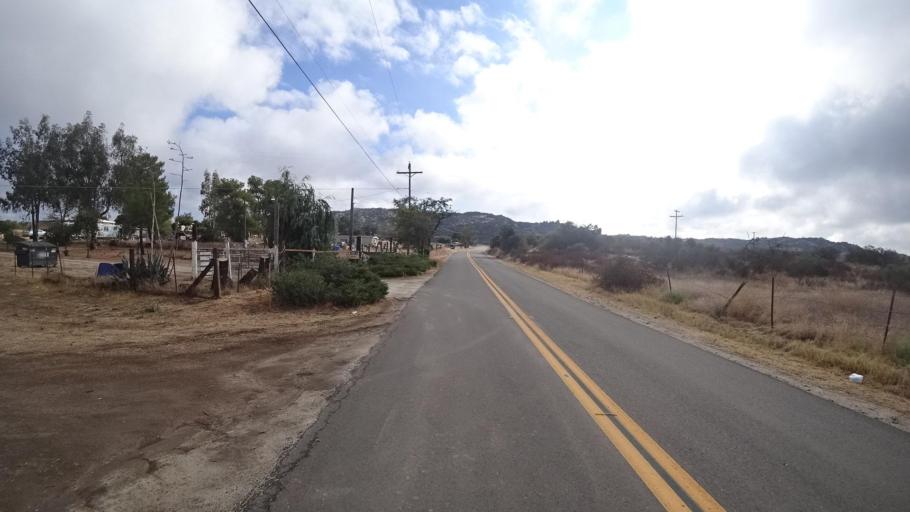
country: MX
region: Baja California
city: Tecate
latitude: 32.6107
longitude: -116.5747
